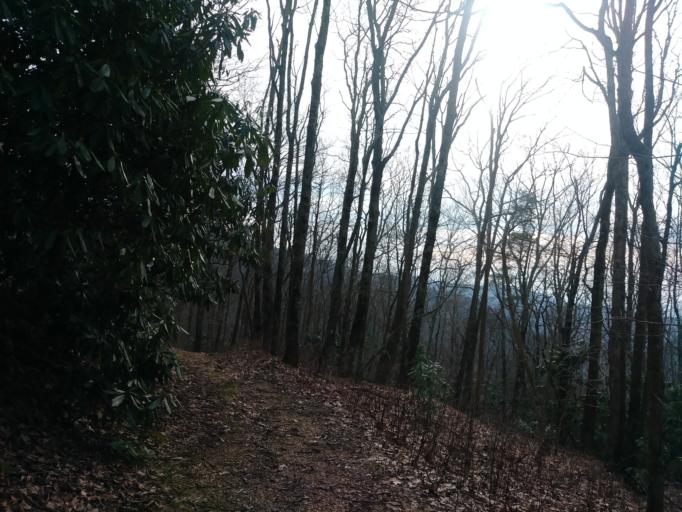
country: US
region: Tennessee
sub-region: Greene County
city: Tusculum
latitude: 36.0544
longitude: -82.6720
